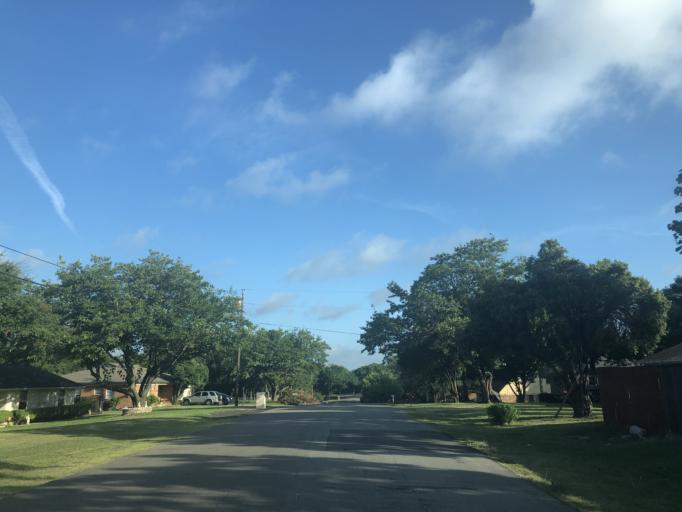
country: US
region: Texas
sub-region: Dallas County
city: Duncanville
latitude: 32.6689
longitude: -96.9105
